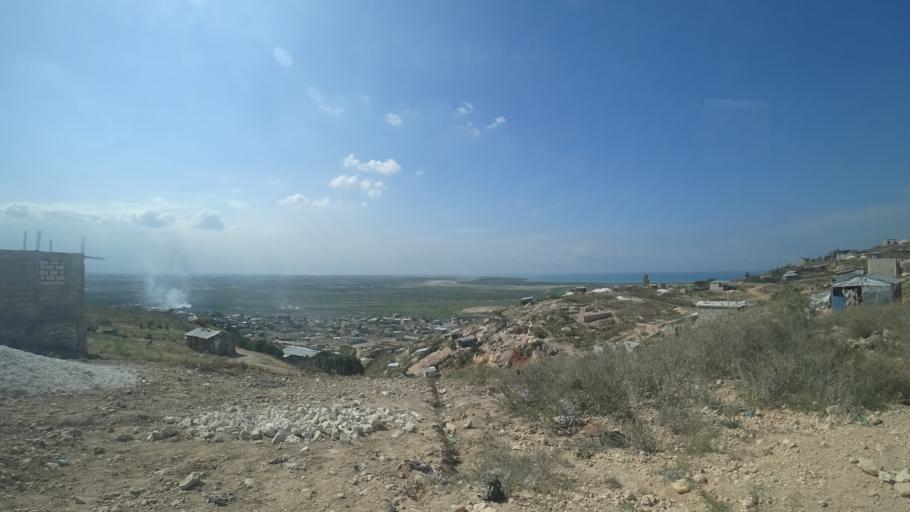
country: HT
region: Ouest
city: Croix des Bouquets
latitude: 18.6688
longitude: -72.2936
